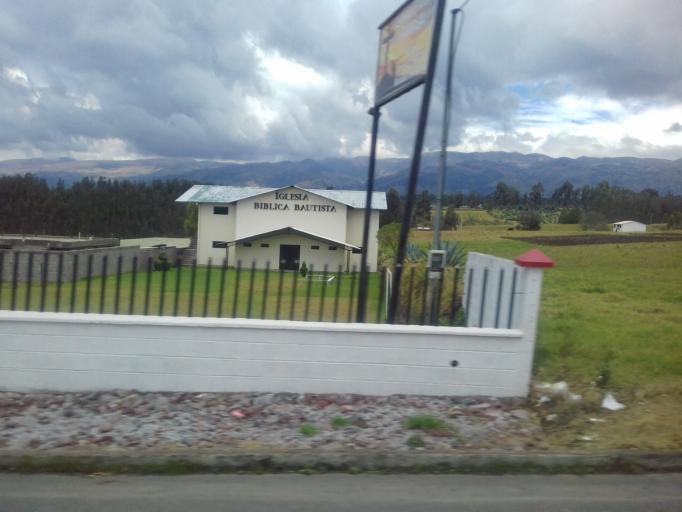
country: EC
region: Pichincha
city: Sangolqui
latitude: -0.3475
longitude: -78.4109
